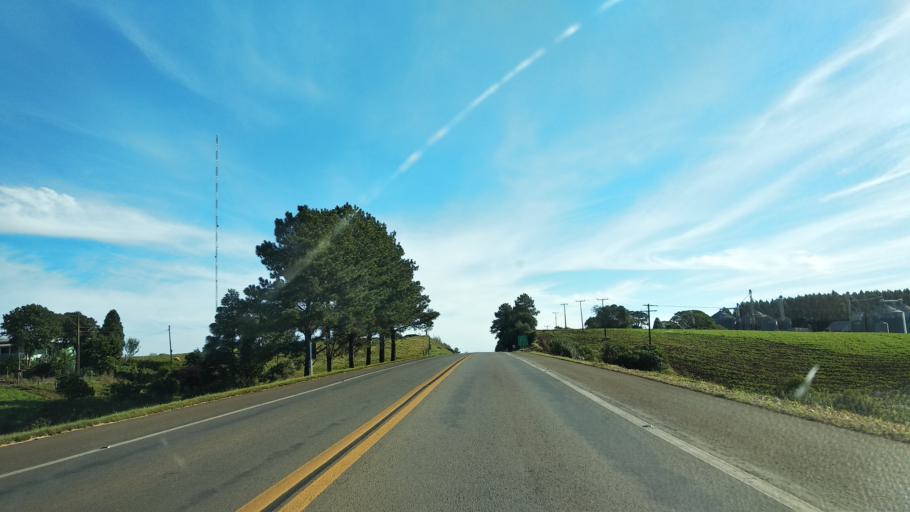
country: BR
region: Santa Catarina
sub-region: Celso Ramos
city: Celso Ramos
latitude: -27.5281
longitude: -51.3813
